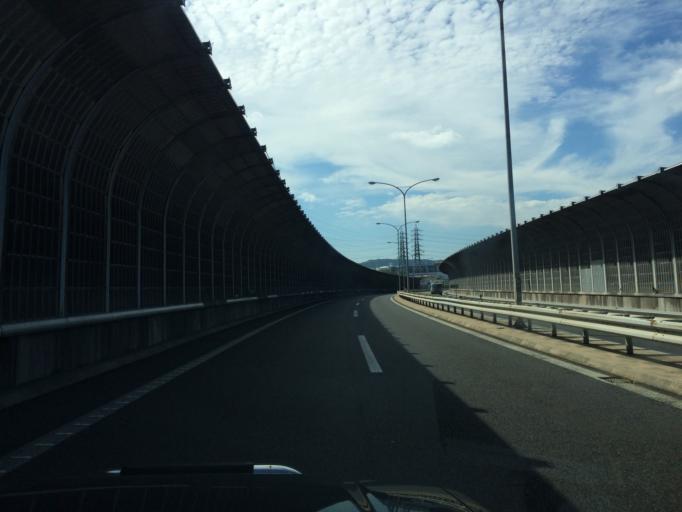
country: JP
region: Osaka
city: Izumi
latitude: 34.4674
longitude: 135.4642
